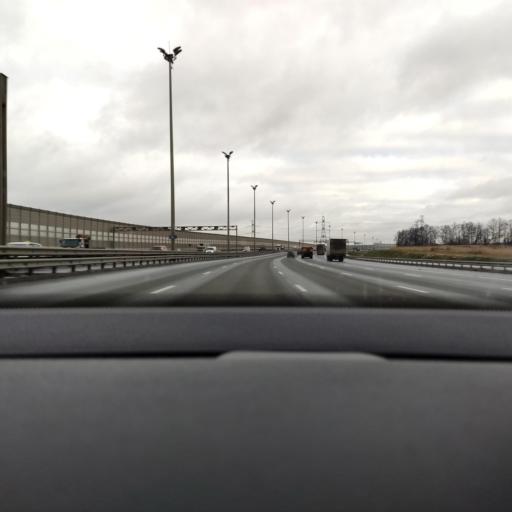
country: RU
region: Moskovskaya
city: Bolshevo
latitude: 55.9477
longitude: 37.8170
